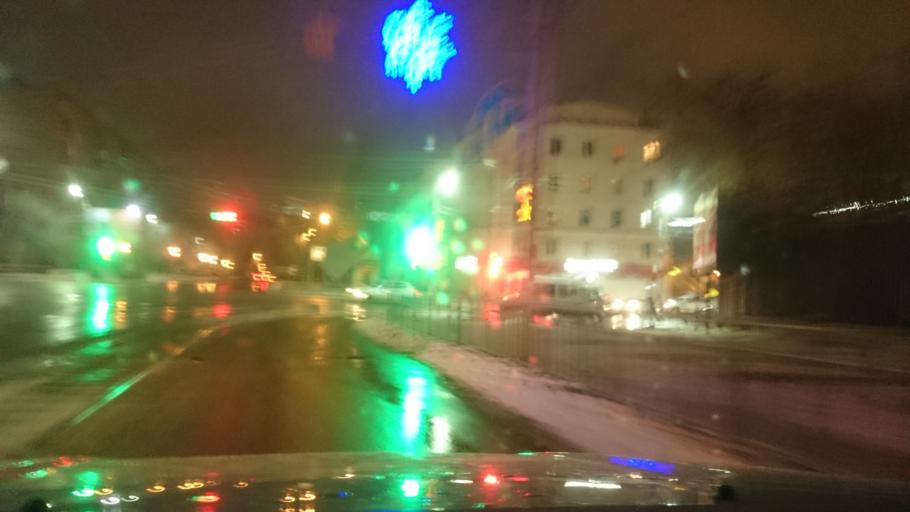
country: RU
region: Tula
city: Tula
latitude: 54.2132
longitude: 37.6216
